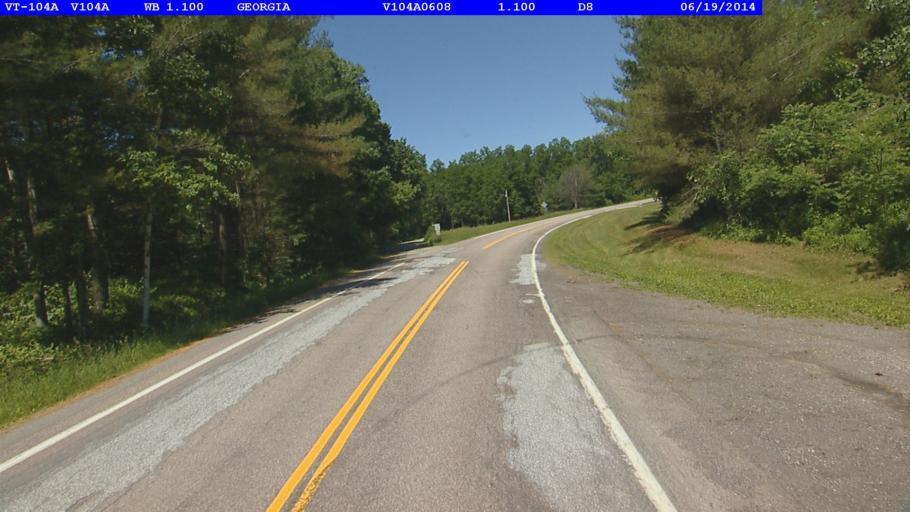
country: US
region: Vermont
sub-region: Chittenden County
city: Milton
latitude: 44.6834
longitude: -73.0935
